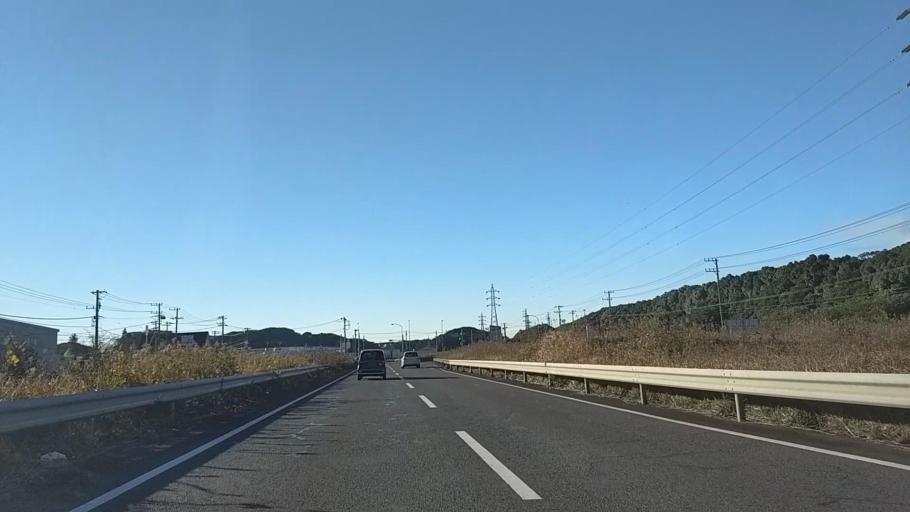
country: JP
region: Chiba
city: Kisarazu
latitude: 35.3645
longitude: 139.9117
